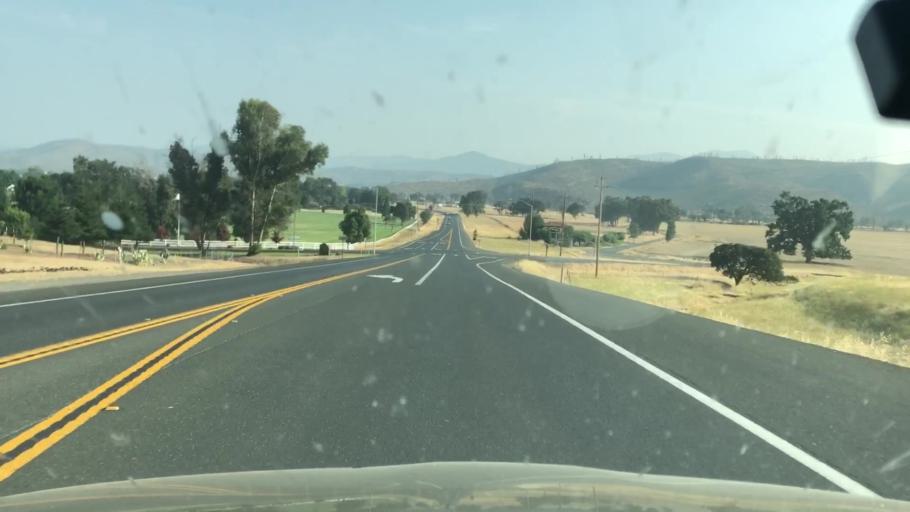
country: US
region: California
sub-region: Lake County
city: Hidden Valley Lake
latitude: 38.8108
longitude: -122.5728
